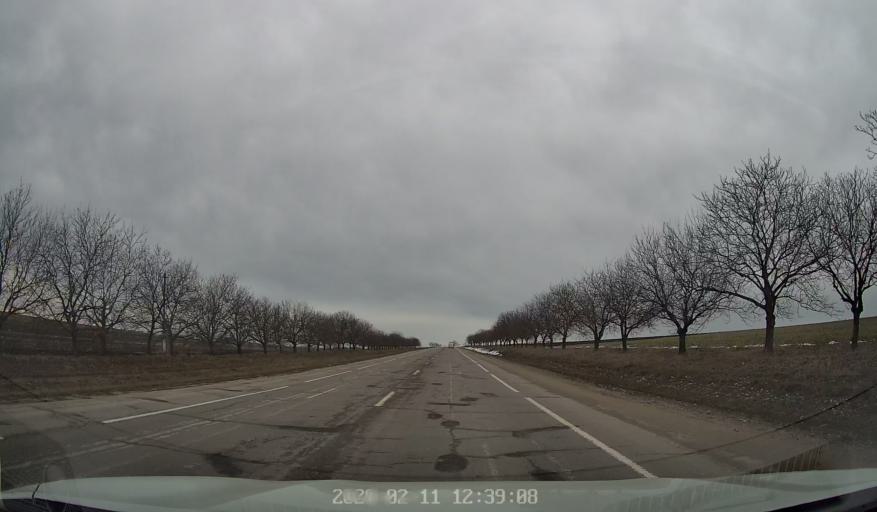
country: MD
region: Raionul Edinet
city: Edinet
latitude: 48.1977
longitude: 27.2751
